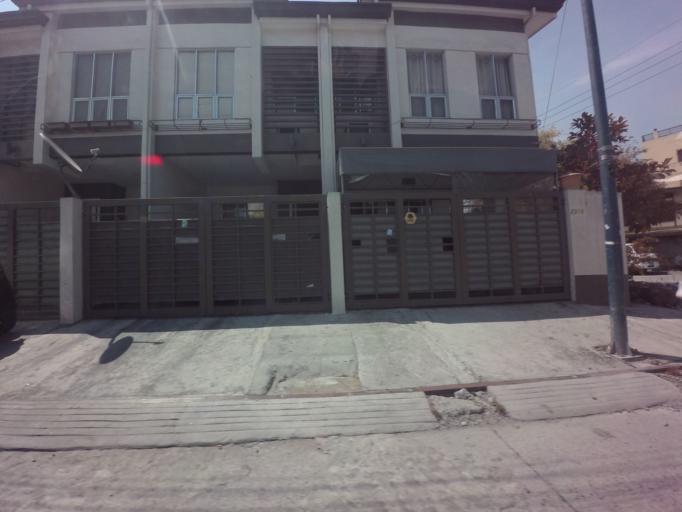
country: PH
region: Metro Manila
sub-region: Makati City
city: Makati City
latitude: 14.5688
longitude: 121.0094
